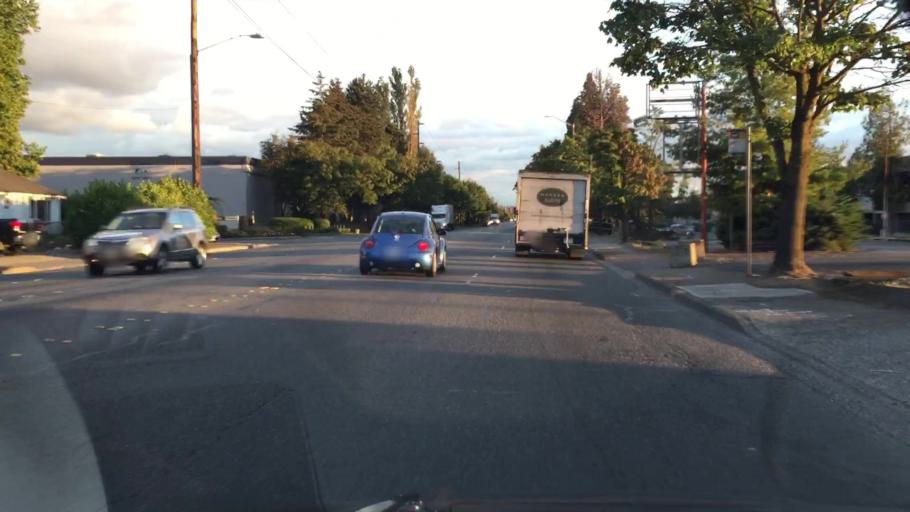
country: US
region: Washington
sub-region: King County
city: Kent
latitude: 47.4257
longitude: -122.2281
